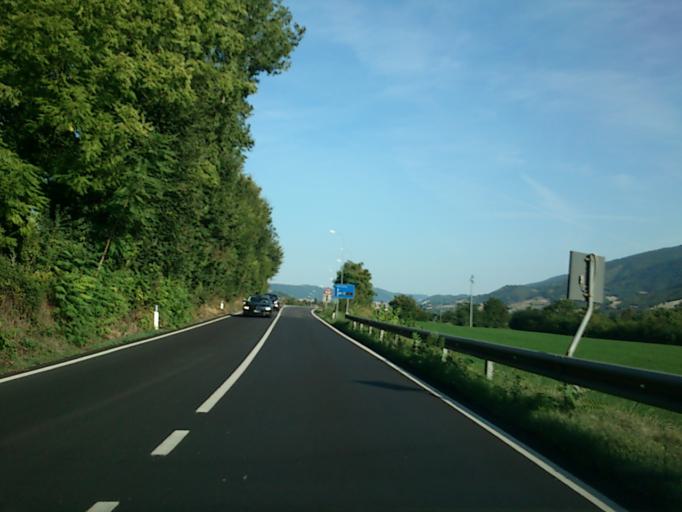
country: IT
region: The Marches
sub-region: Provincia di Pesaro e Urbino
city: Canavaccio
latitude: 43.6998
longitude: 12.6854
